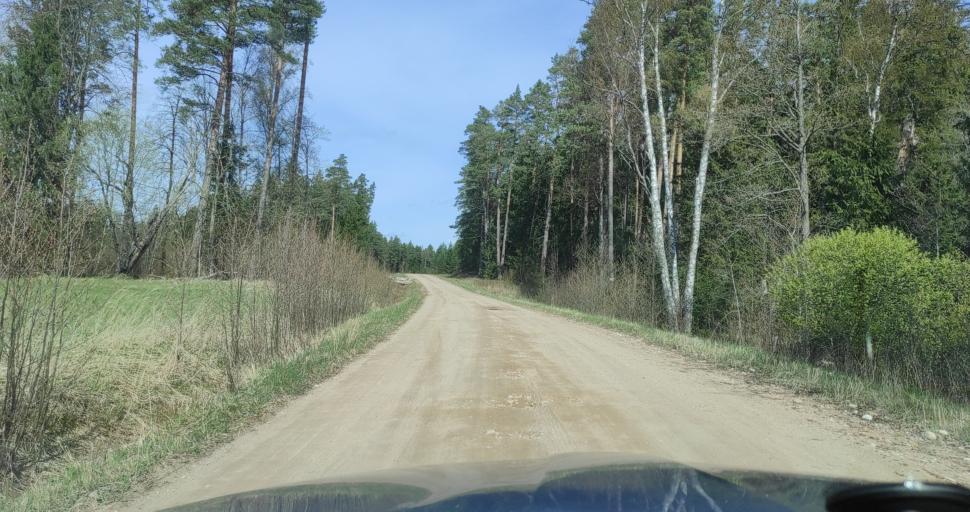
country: LV
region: Talsu Rajons
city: Stende
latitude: 57.1249
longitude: 22.2731
